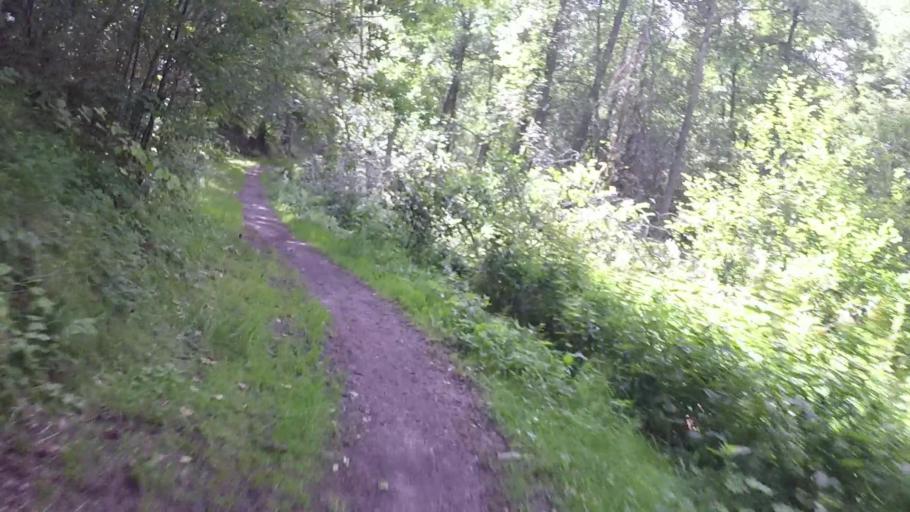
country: SE
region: Vaestra Goetaland
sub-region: Trollhattan
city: Trollhattan
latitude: 58.2527
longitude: 12.2677
